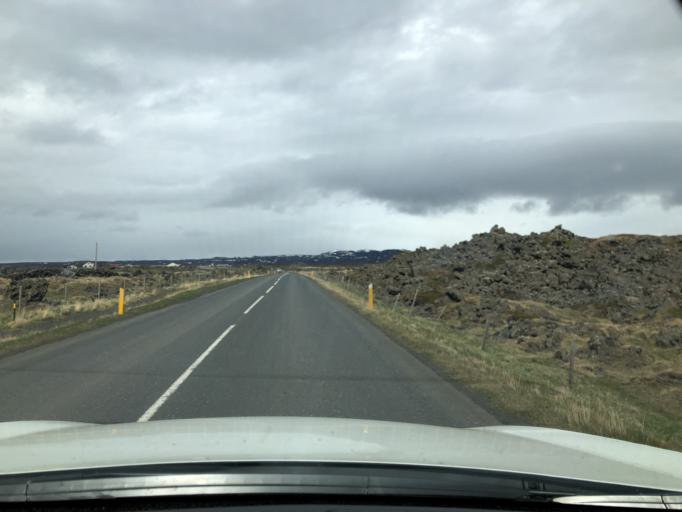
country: IS
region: Northeast
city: Laugar
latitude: 65.6145
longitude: -16.9156
